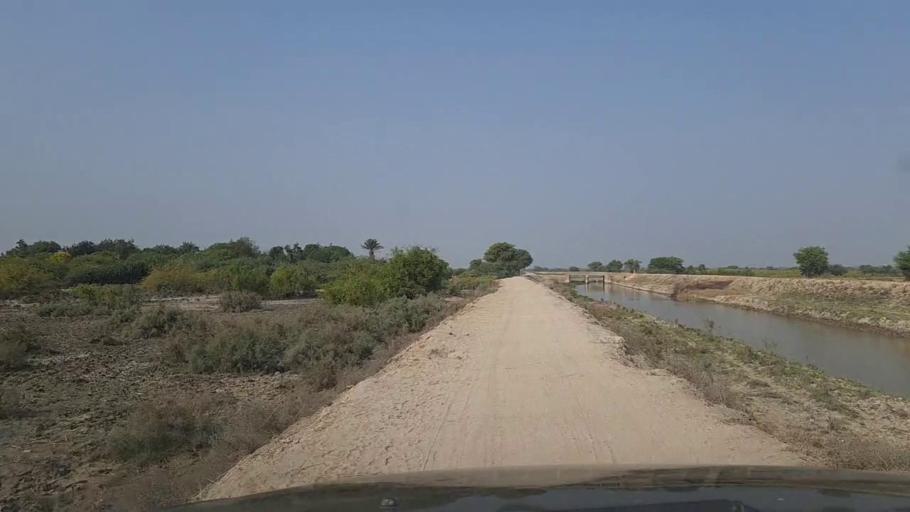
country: PK
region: Sindh
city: Mirpur Batoro
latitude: 24.6791
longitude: 68.2487
